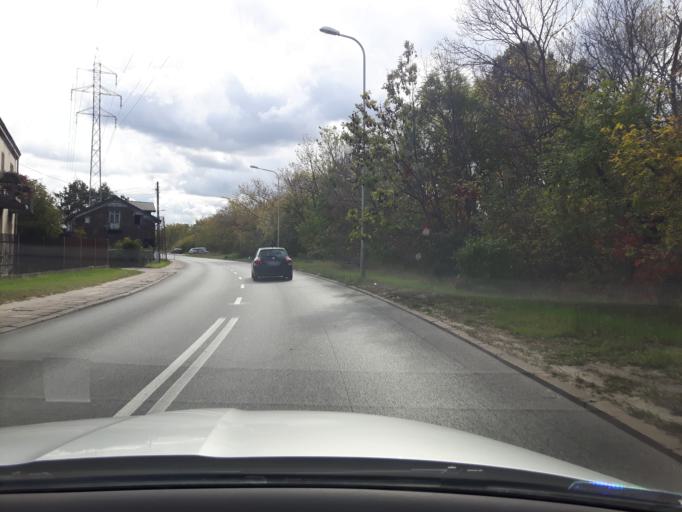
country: PL
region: Masovian Voivodeship
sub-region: Warszawa
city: Rembertow
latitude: 52.2301
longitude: 21.1438
